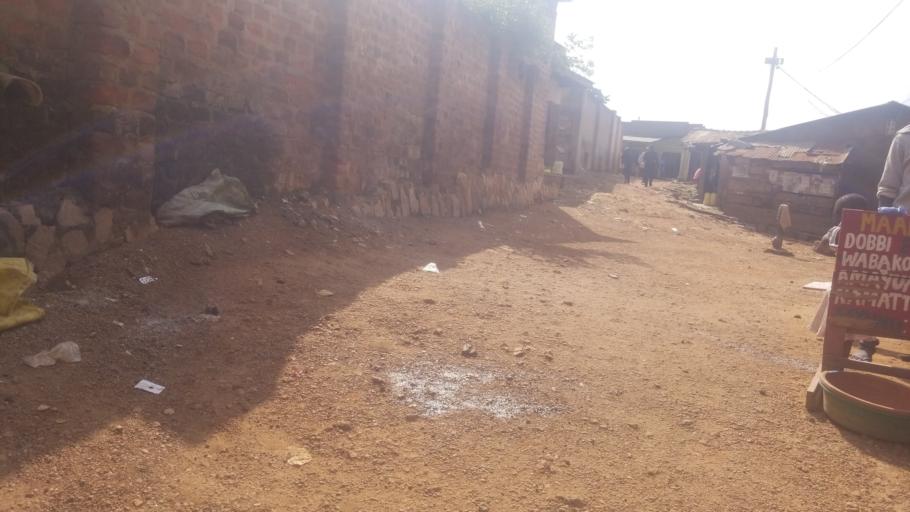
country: UG
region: Central Region
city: Kampala Central Division
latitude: 0.3324
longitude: 32.5597
